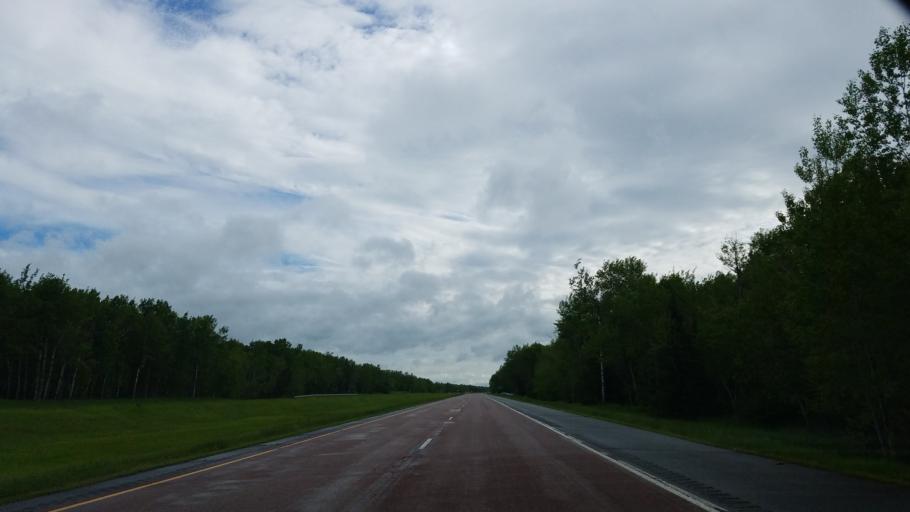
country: US
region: Minnesota
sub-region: Saint Louis County
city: Arnold
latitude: 46.8748
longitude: -91.9475
